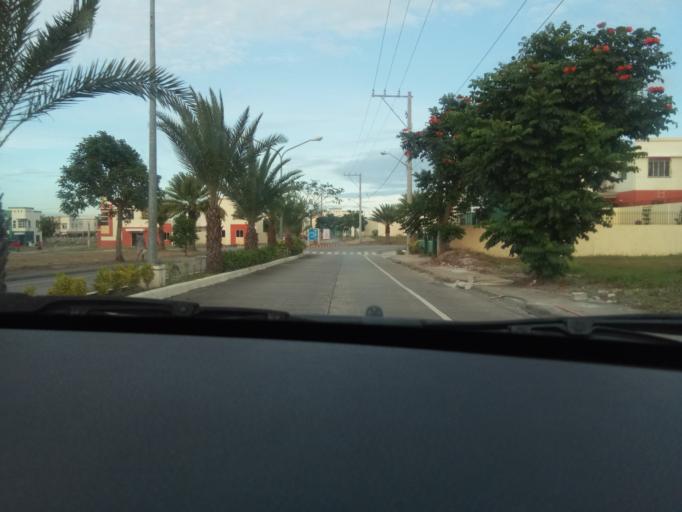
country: PH
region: Calabarzon
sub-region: Province of Cavite
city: Biga
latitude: 14.2755
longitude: 120.9672
